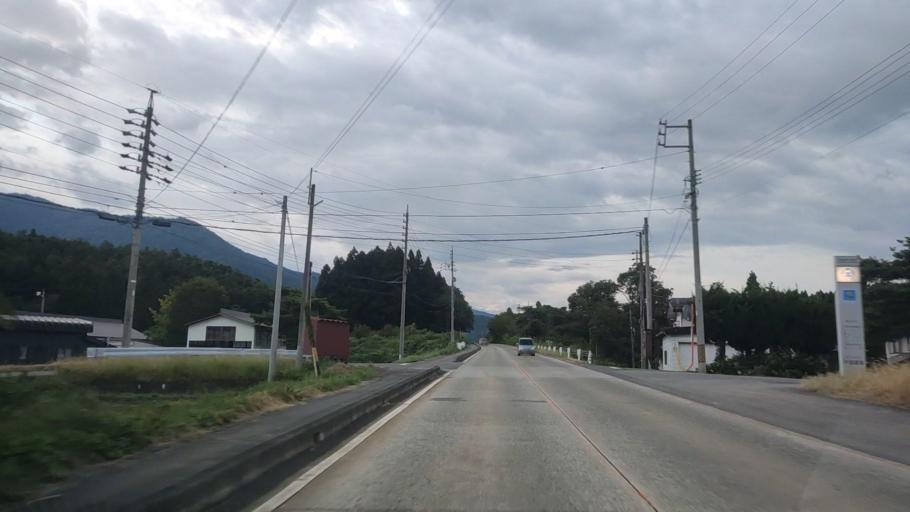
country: JP
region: Nagano
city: Iiyama
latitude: 36.8903
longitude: 138.4078
